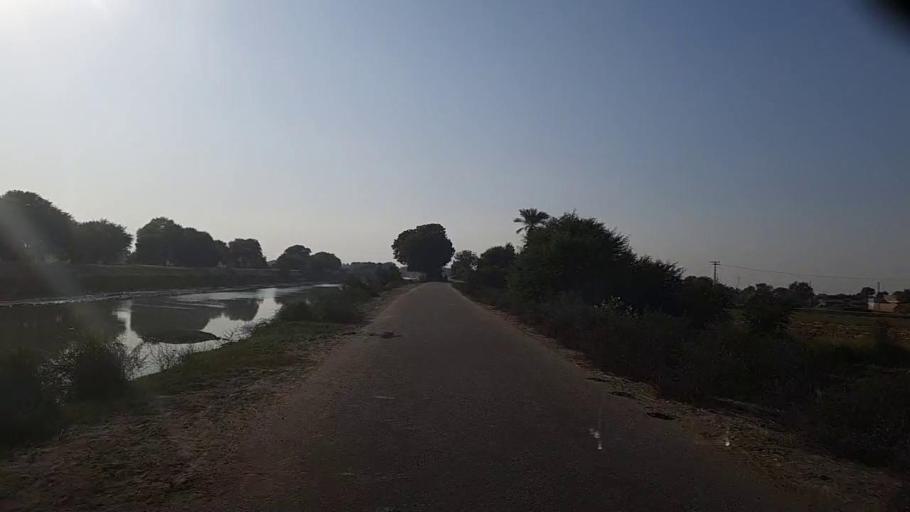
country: PK
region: Sindh
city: Tangwani
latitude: 28.3013
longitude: 68.9347
